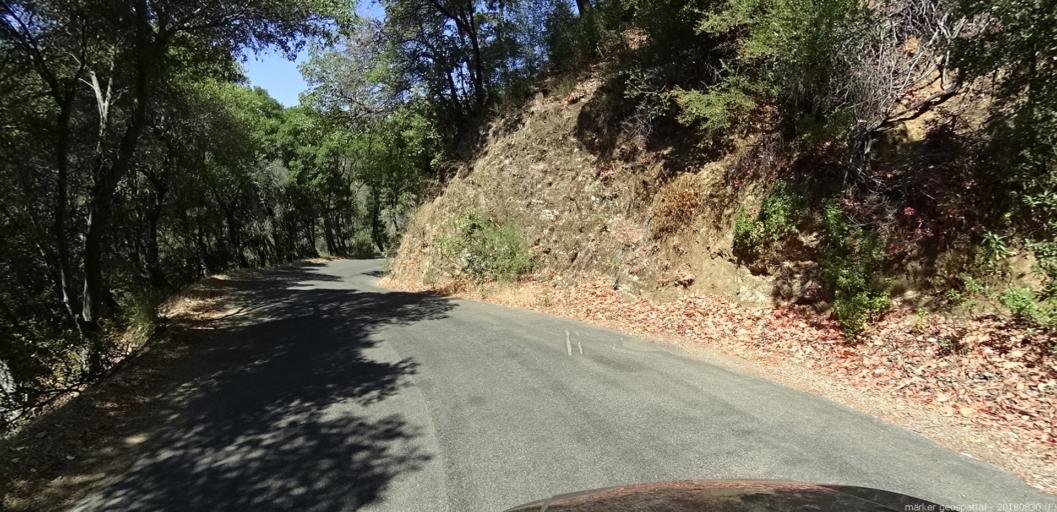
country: US
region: California
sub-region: Monterey County
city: Greenfield
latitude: 36.0123
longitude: -121.4408
